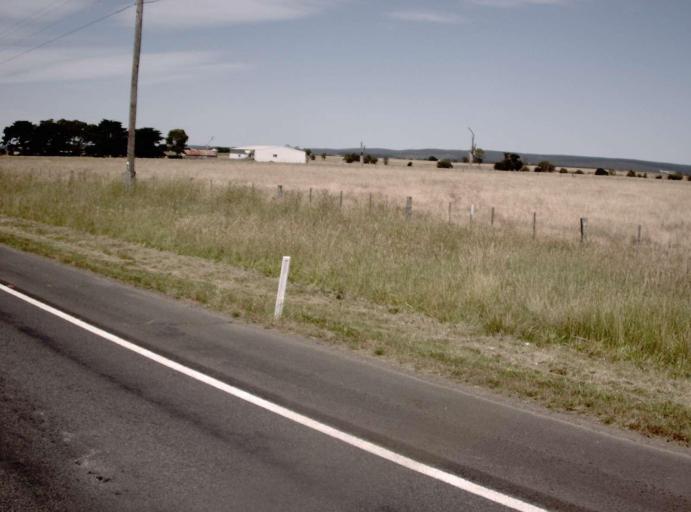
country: AU
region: Victoria
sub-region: Wellington
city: Heyfield
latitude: -38.1585
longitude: 146.7384
